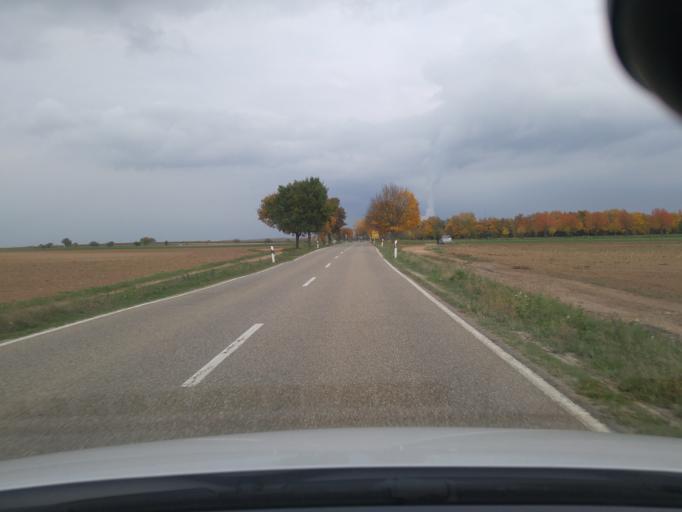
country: DE
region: Rheinland-Pfalz
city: Lingenfeld
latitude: 49.2684
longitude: 8.3730
